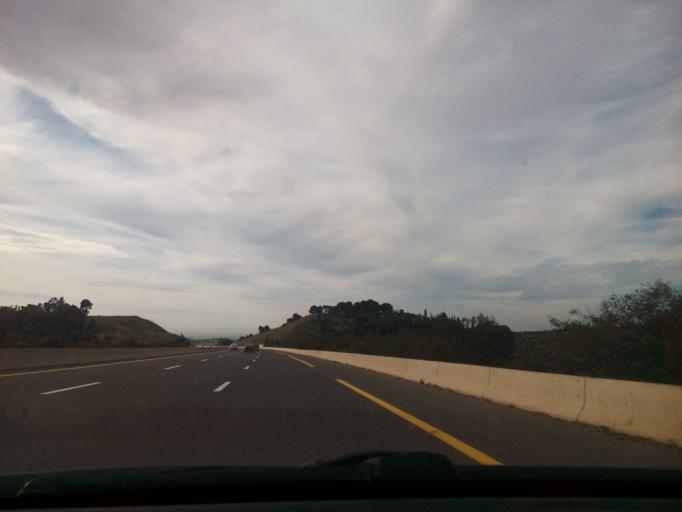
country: DZ
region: Sidi Bel Abbes
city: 'Ain el Berd
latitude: 35.3549
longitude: -0.5116
